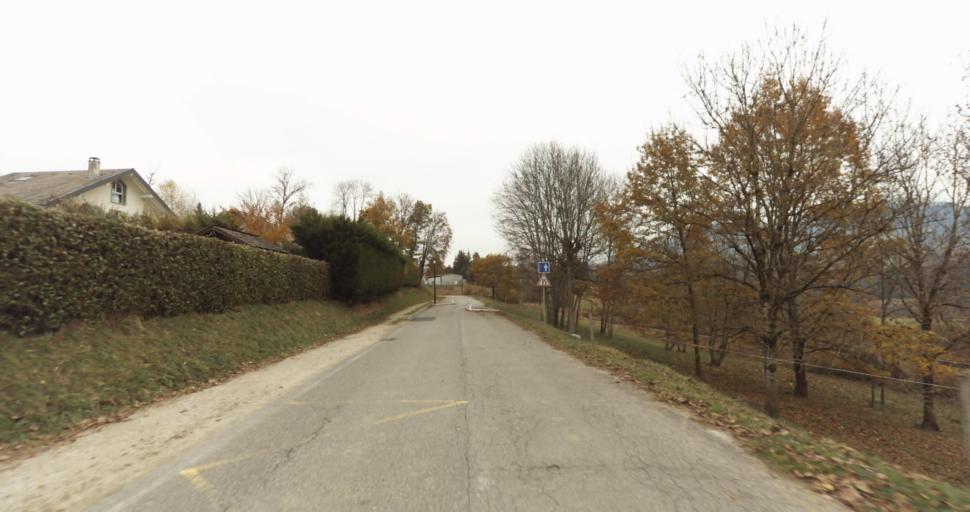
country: FR
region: Rhone-Alpes
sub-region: Departement de la Haute-Savoie
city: Saint-Martin-Bellevue
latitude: 45.9474
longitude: 6.1544
